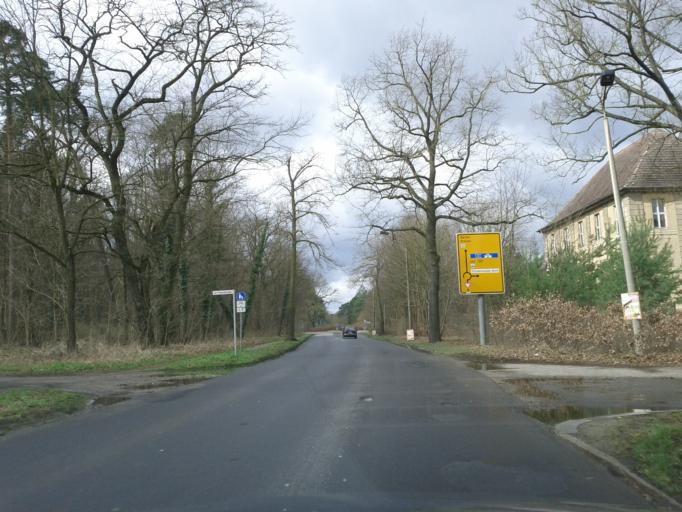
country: DE
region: Brandenburg
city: Furstenwalde
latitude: 52.3667
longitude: 14.0446
